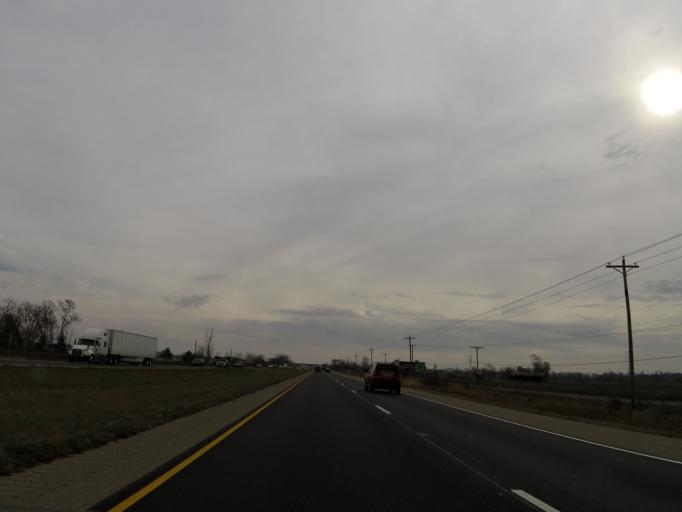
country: US
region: Indiana
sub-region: Shelby County
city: Shelbyville
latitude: 39.5687
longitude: -85.8014
